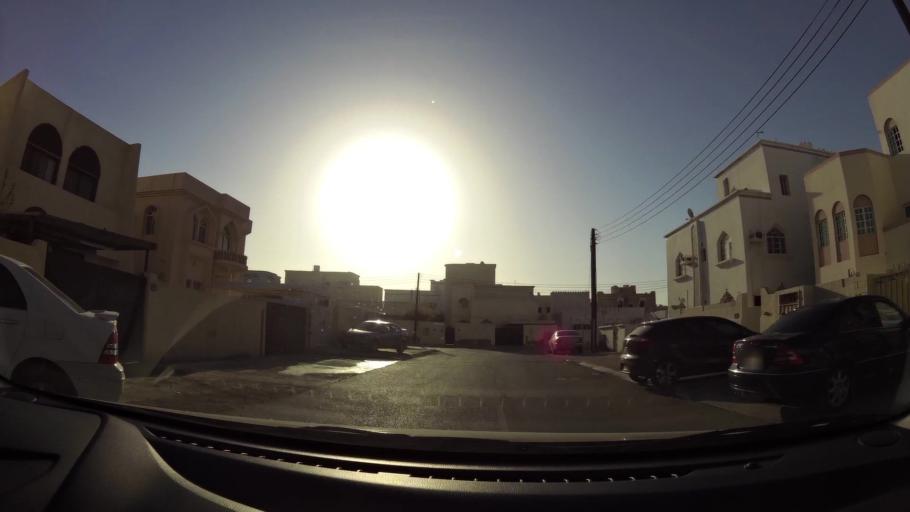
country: OM
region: Muhafazat Masqat
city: As Sib al Jadidah
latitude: 23.6293
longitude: 58.1939
